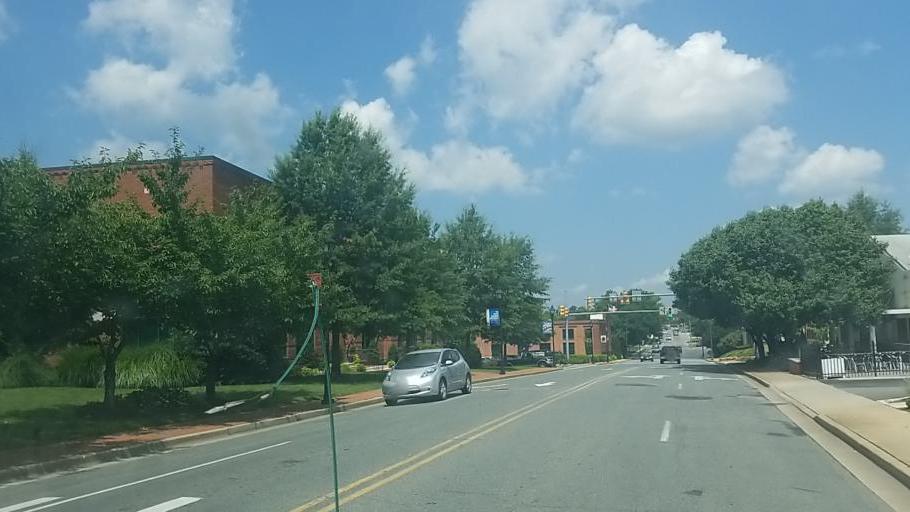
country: US
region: Maryland
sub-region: Talbot County
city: Easton
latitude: 38.7772
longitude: -76.0762
